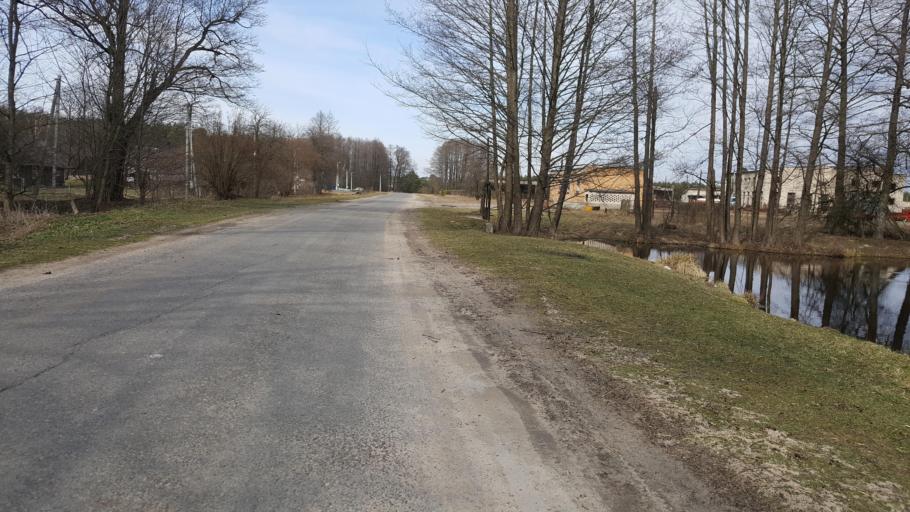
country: BY
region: Brest
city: Kamyanyets
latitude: 52.3952
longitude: 24.0031
